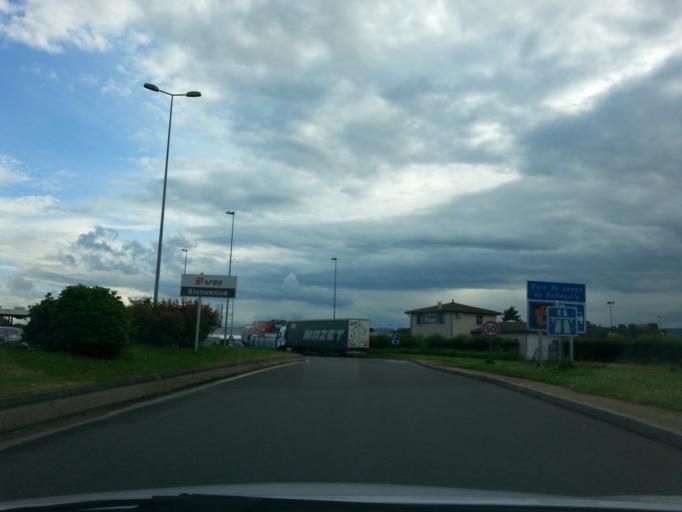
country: FR
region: Rhone-Alpes
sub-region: Departement du Rhone
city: Belleville
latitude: 46.1052
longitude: 4.7510
